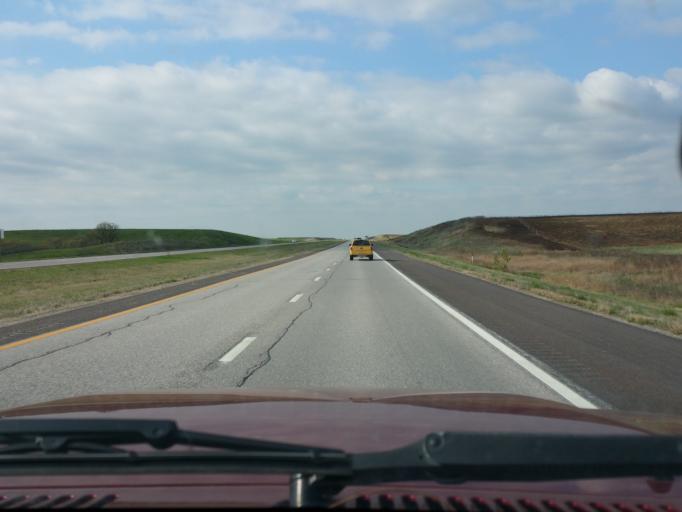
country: US
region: Kansas
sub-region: Riley County
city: Manhattan
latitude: 39.1102
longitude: -96.5381
